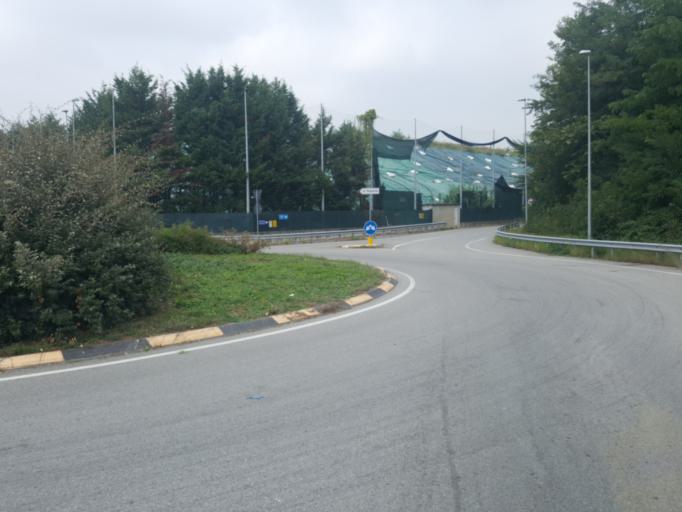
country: IT
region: Lombardy
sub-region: Provincia di Como
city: Carbonate
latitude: 45.6658
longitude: 8.9258
